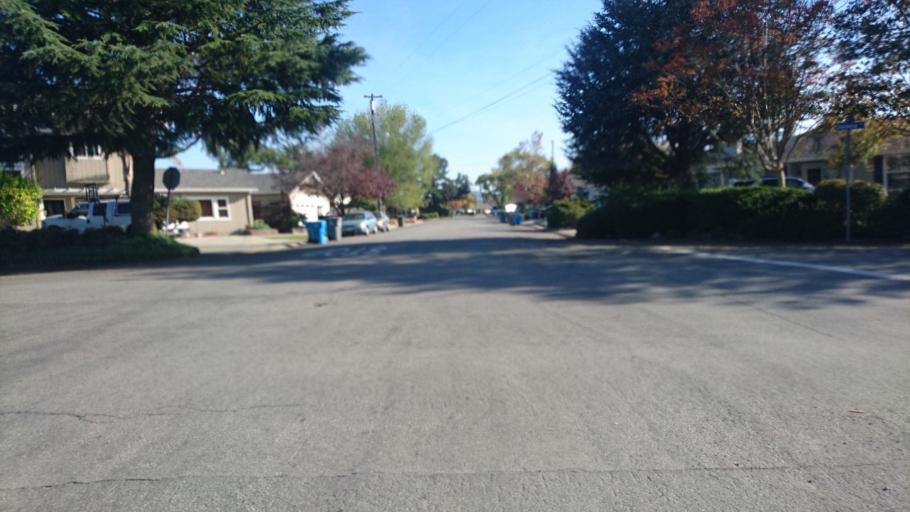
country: US
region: California
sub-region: Santa Clara County
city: Cambrian Park
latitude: 37.2578
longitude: -121.9249
